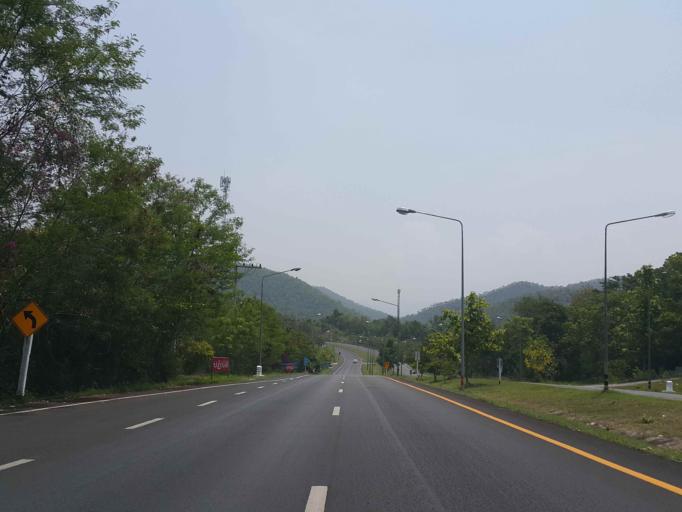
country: TH
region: Chiang Mai
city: San Sai
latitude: 18.8879
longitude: 99.1625
